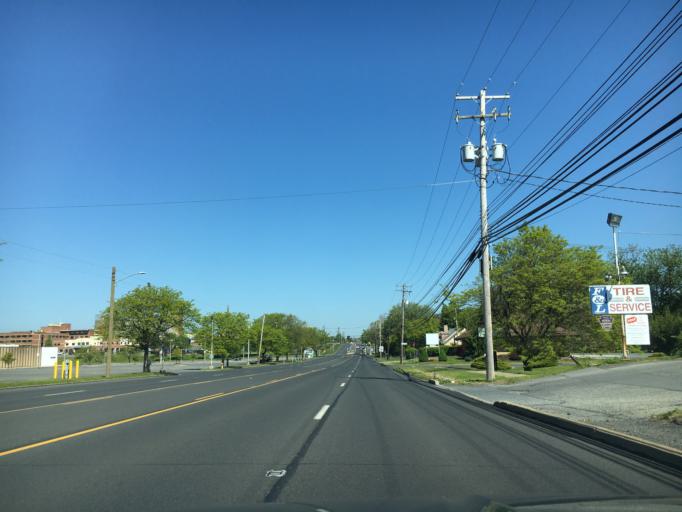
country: US
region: Pennsylvania
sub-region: Northampton County
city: Bethlehem
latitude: 40.6425
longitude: -75.4025
